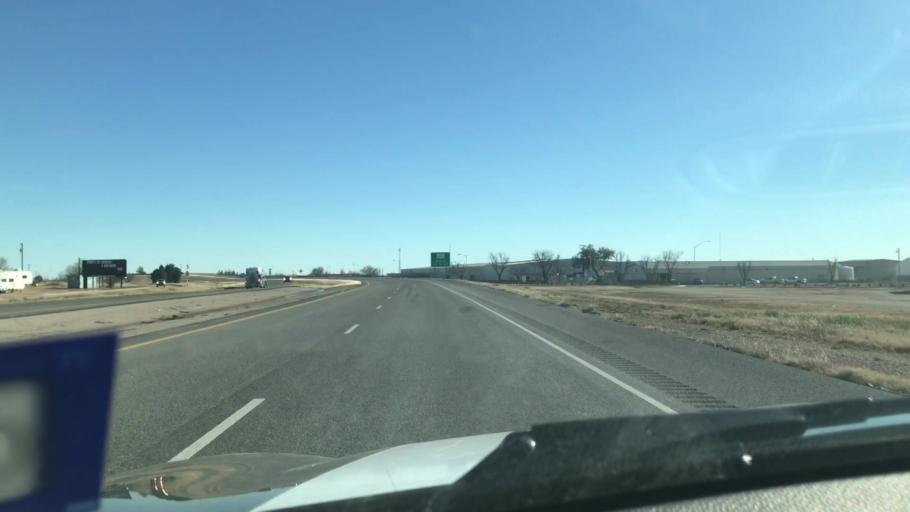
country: US
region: Texas
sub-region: Scurry County
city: Snyder
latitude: 32.7438
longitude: -100.9228
